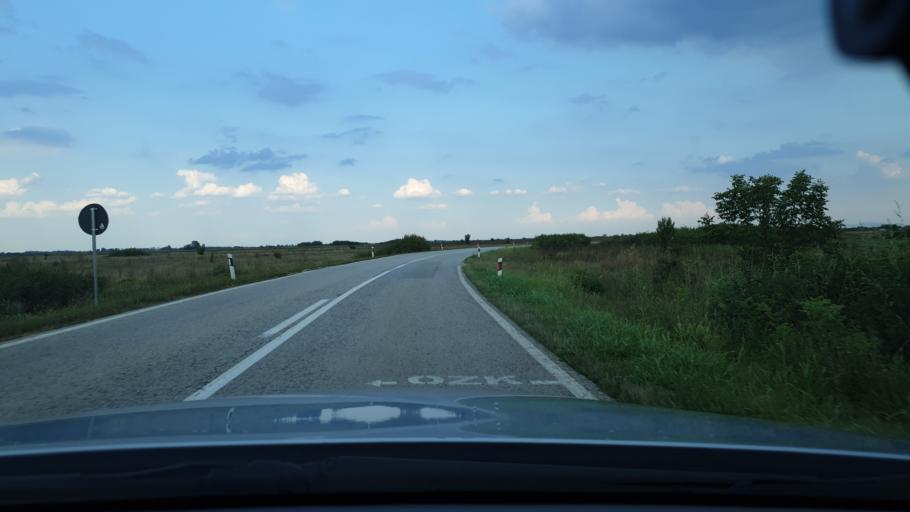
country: RS
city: Konak
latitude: 45.3301
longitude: 20.8923
